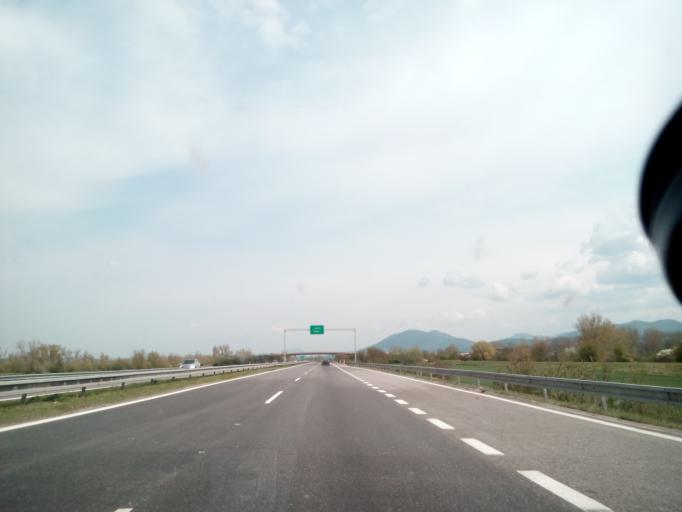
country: SK
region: Nitriansky
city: Dubnica nad Vahom
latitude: 48.9843
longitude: 18.1913
